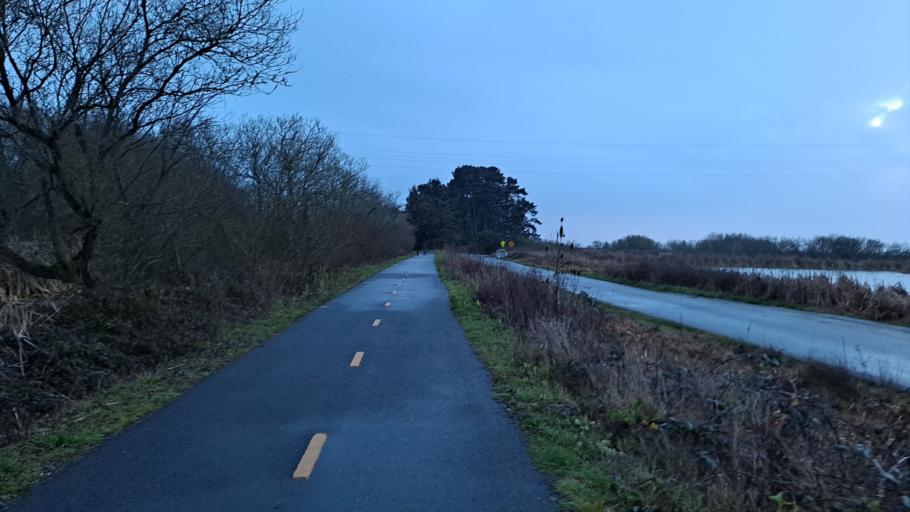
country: US
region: California
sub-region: Humboldt County
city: Arcata
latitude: 40.8600
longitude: -124.0939
